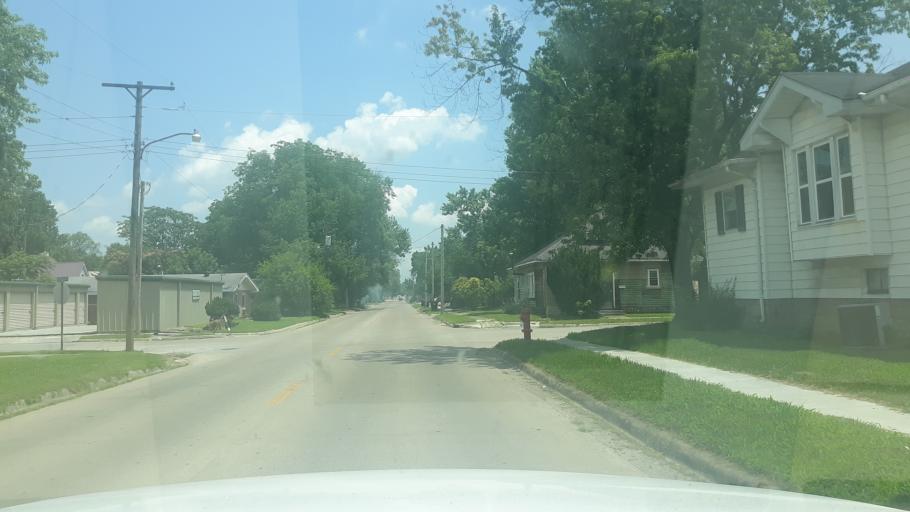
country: US
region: Illinois
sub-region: Saline County
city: Harrisburg
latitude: 37.7312
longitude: -88.5441
